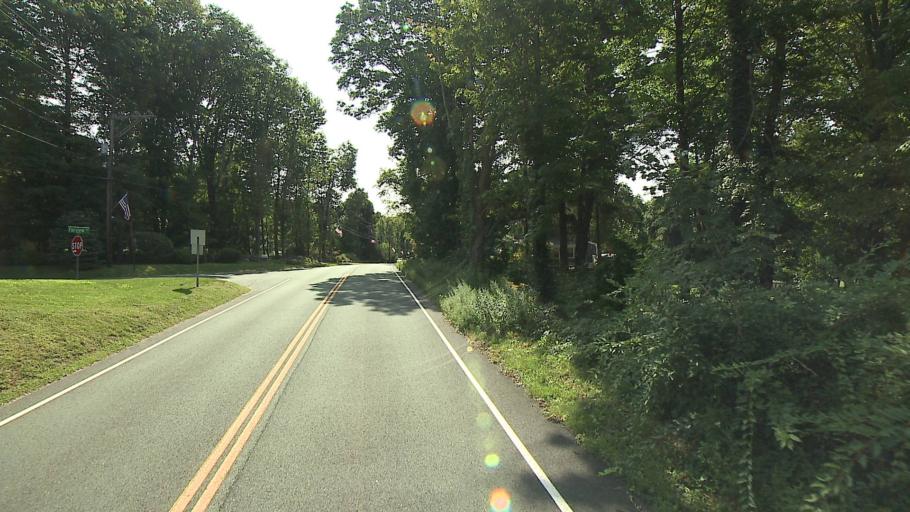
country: US
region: Connecticut
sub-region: Fairfield County
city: Danbury
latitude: 41.4771
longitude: -73.3990
